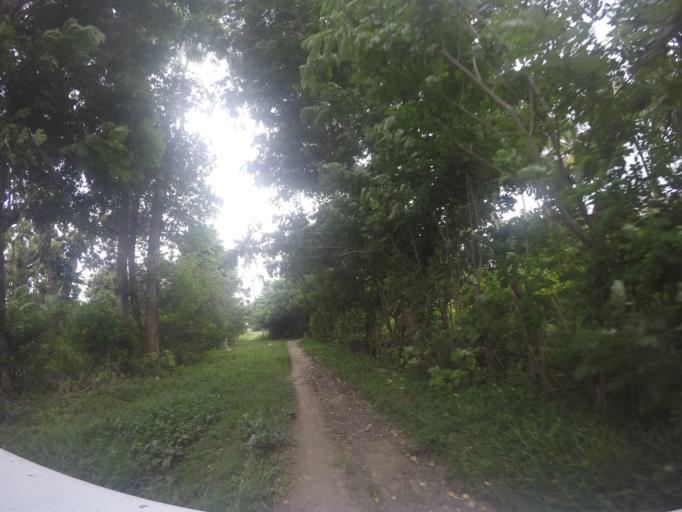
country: TL
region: Lautem
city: Lospalos
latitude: -8.5167
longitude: 126.9912
